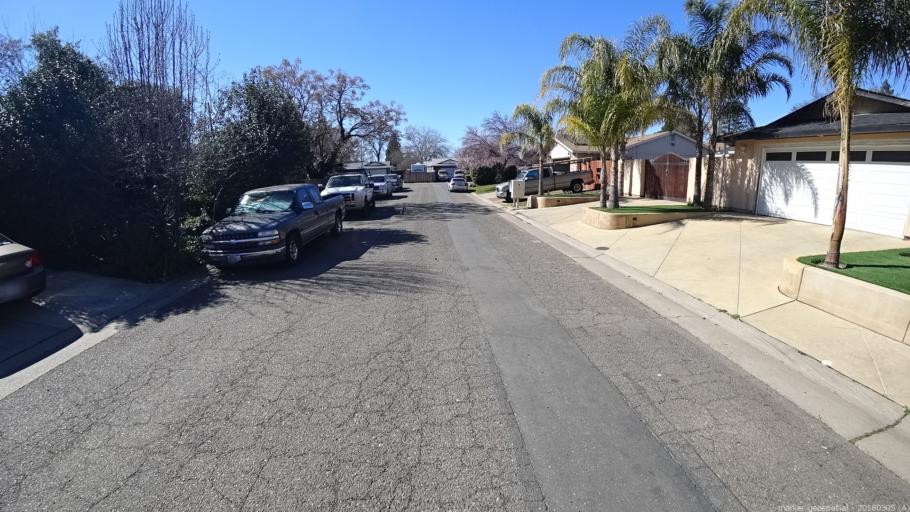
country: US
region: California
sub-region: Sacramento County
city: Florin
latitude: 38.4912
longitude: -121.3820
